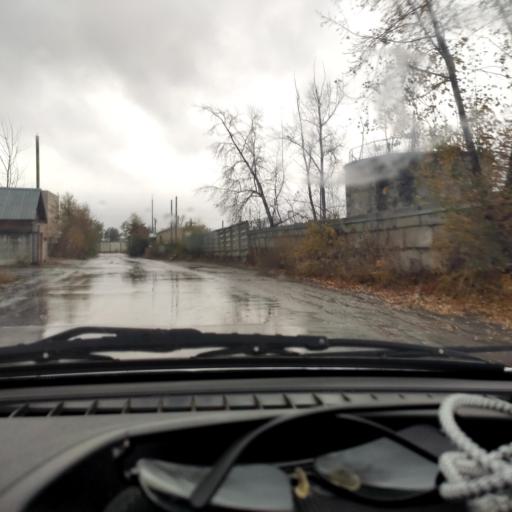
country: RU
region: Samara
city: Zhigulevsk
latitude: 53.4652
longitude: 49.5659
